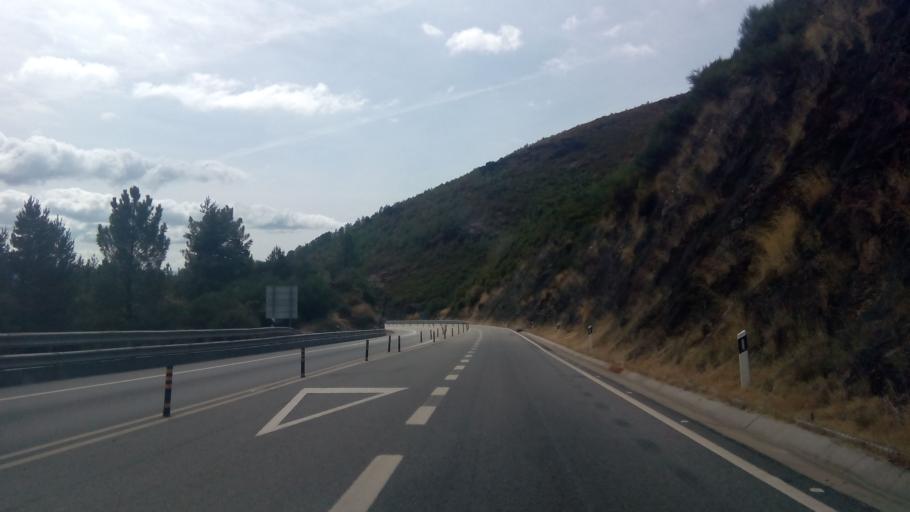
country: PT
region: Vila Real
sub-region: Mesao Frio
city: Mesao Frio
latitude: 41.2715
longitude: -7.9410
